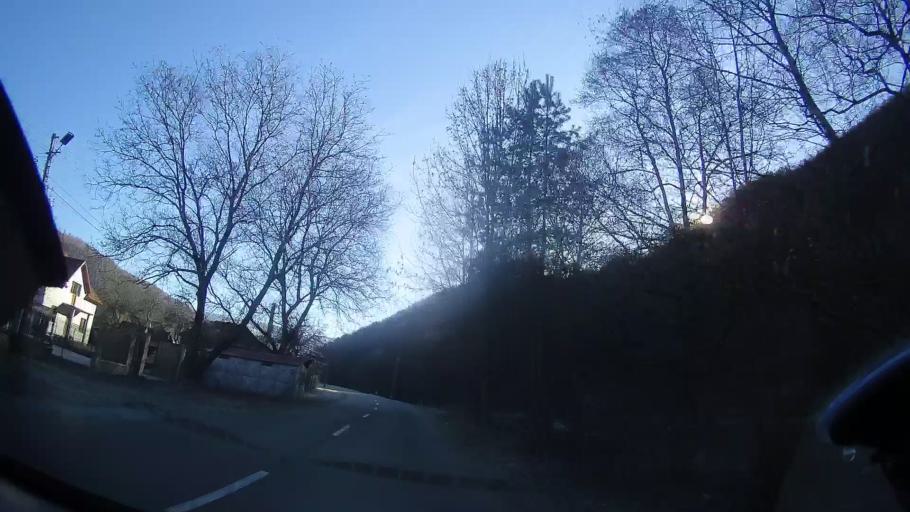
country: RO
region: Bihor
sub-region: Comuna Bulz
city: Bulz
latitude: 46.9086
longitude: 22.6795
